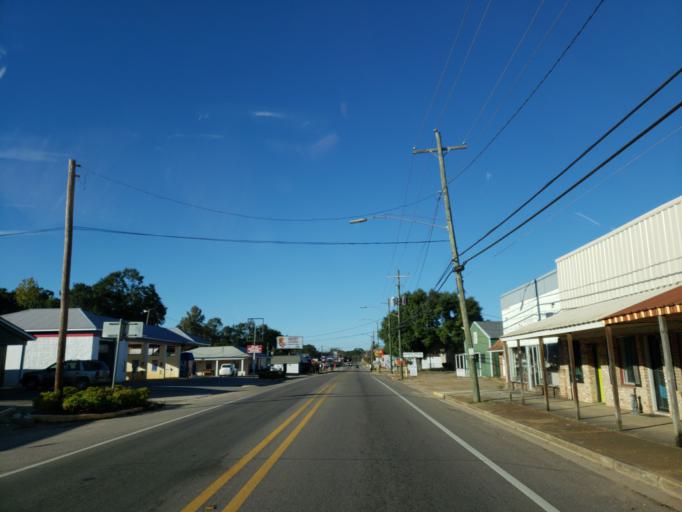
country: US
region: Mississippi
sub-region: Perry County
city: Richton
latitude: 31.3492
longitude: -88.9358
